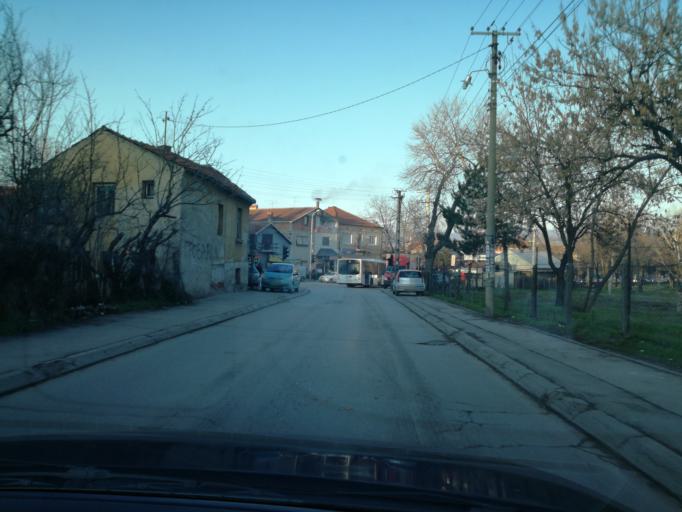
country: RS
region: Central Serbia
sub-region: Nisavski Okrug
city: Nis
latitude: 43.3114
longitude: 21.8768
